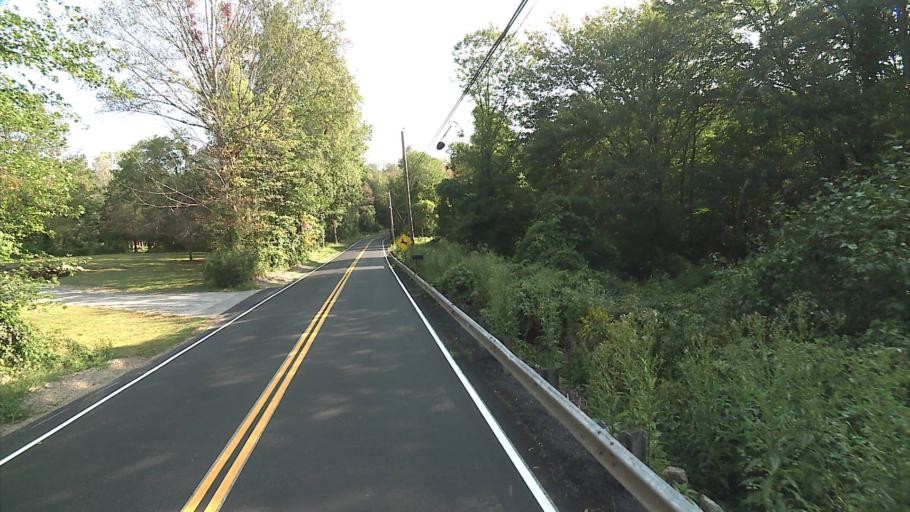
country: US
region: Connecticut
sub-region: Tolland County
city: Coventry Lake
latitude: 41.7296
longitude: -72.3896
